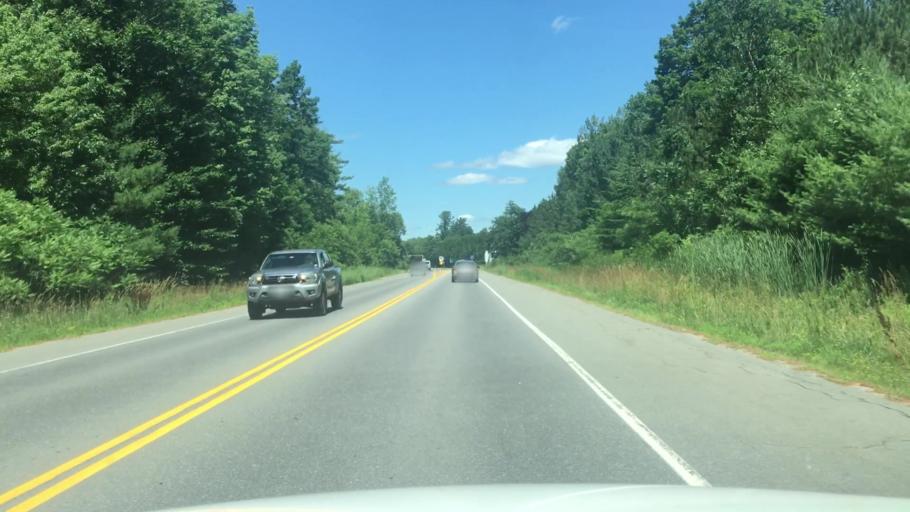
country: US
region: Maine
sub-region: Kennebec County
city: Waterville
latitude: 44.5371
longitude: -69.6495
